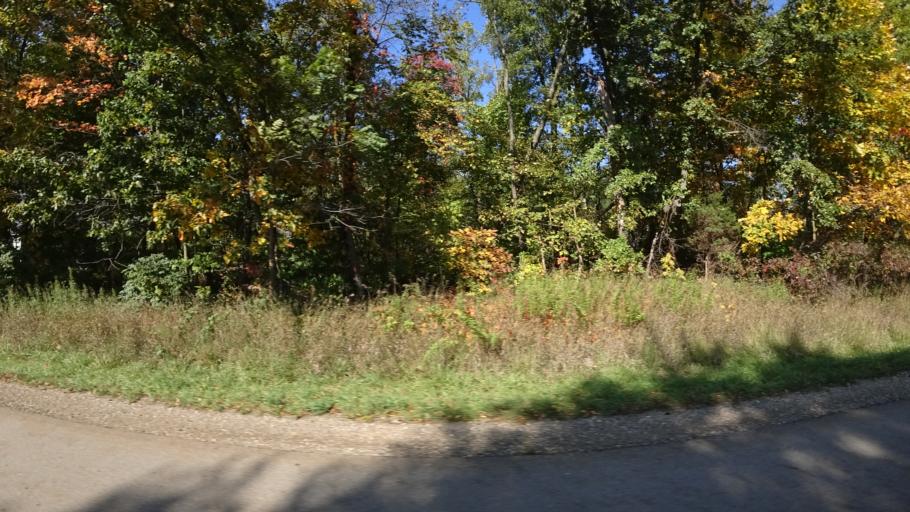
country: US
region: Michigan
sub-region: Jackson County
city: Spring Arbor
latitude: 42.1956
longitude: -84.5959
